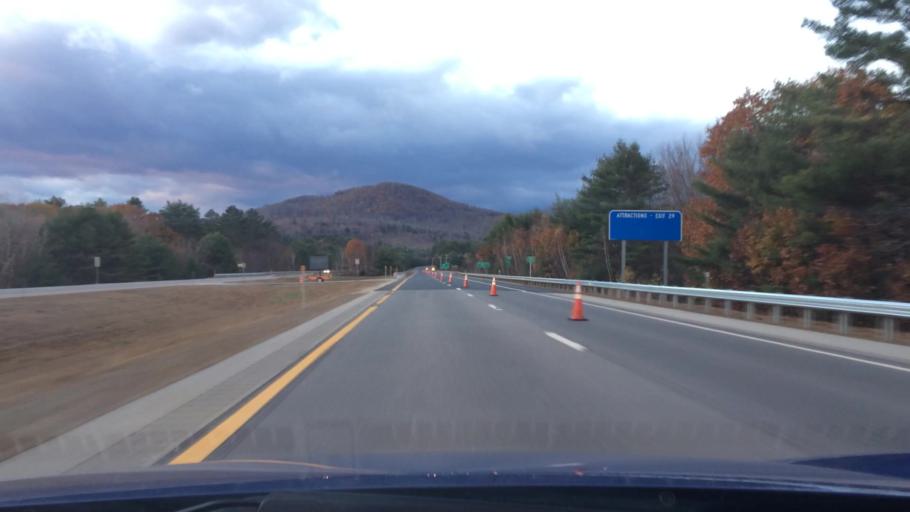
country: US
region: New Hampshire
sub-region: Grafton County
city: Thornton
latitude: 43.8661
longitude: -71.6616
